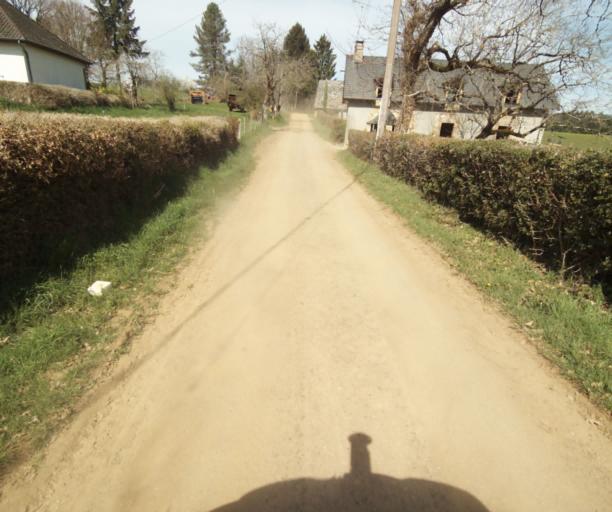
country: FR
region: Limousin
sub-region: Departement de la Correze
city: Seilhac
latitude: 45.4051
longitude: 1.7743
